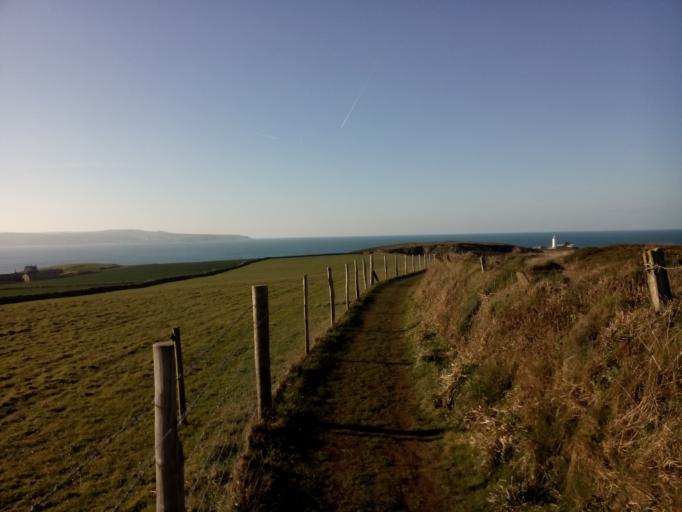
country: GB
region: England
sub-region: Cornwall
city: Hayle
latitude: 50.2394
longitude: -5.3849
